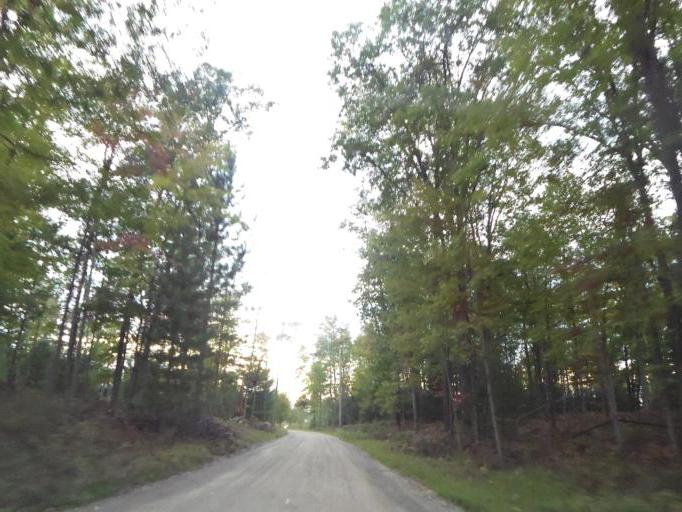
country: US
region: Michigan
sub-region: Roscommon County
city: Saint Helen
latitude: 44.3579
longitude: -84.4698
